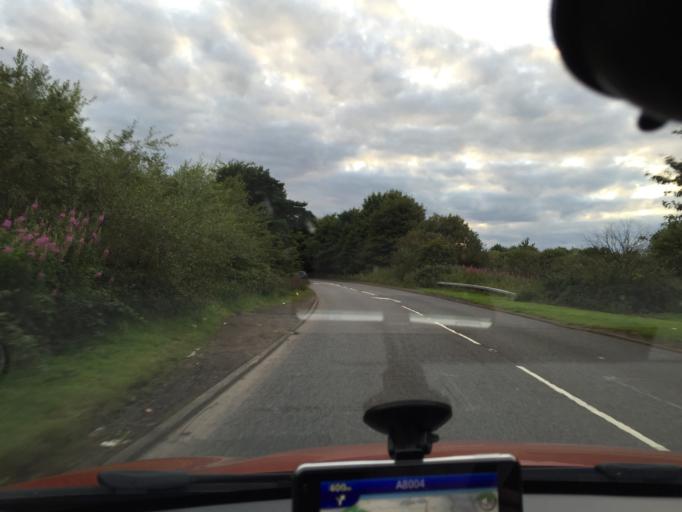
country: GB
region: Scotland
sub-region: Falkirk
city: Bonnybridge
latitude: 56.0128
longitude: -3.8735
